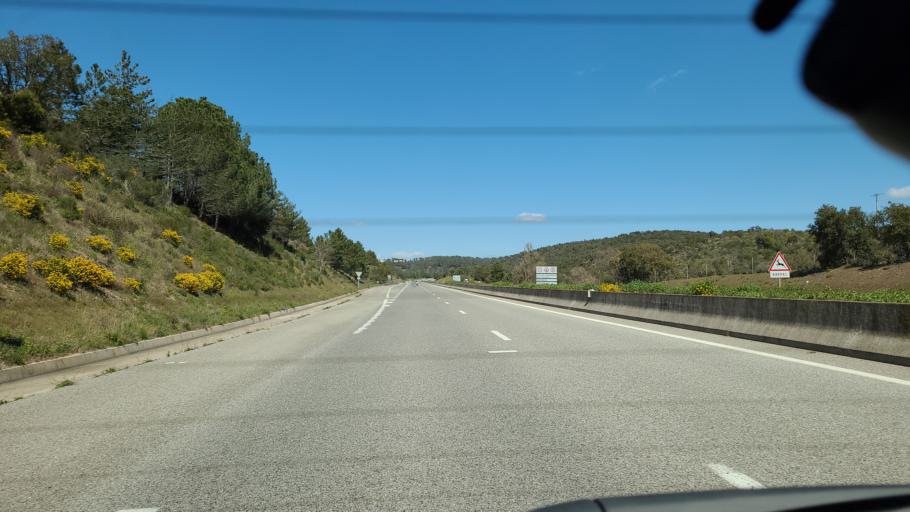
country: FR
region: Provence-Alpes-Cote d'Azur
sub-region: Departement du Var
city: Carnoules
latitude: 43.2771
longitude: 6.1870
